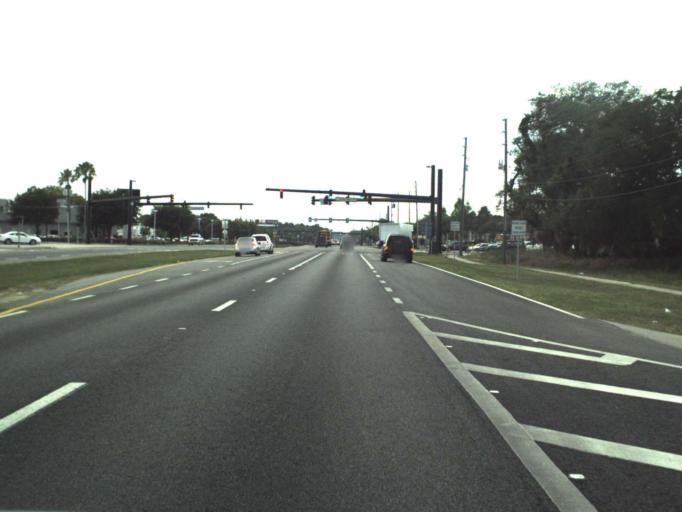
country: US
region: Florida
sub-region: Seminole County
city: Lake Mary
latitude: 28.7341
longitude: -81.3068
